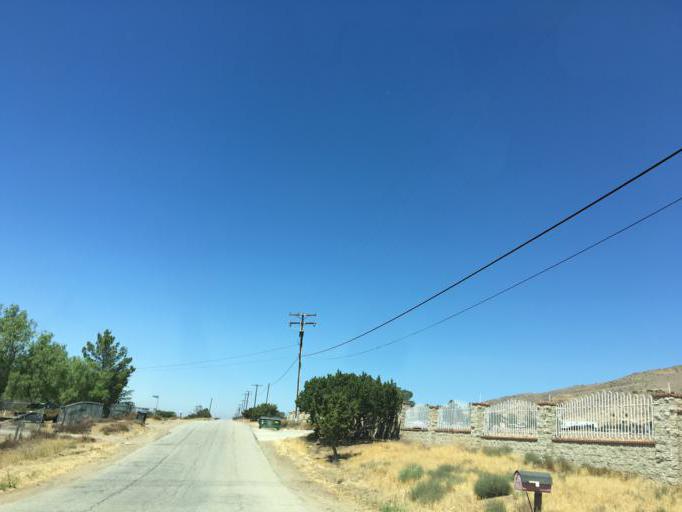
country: US
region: California
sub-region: Los Angeles County
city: Acton
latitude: 34.5245
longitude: -118.2303
